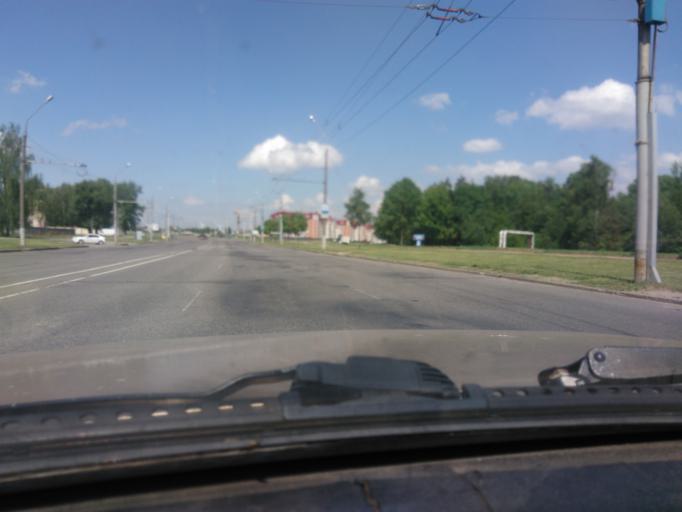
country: BY
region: Mogilev
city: Palykavichy Pyershyya
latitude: 53.9575
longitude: 30.3634
